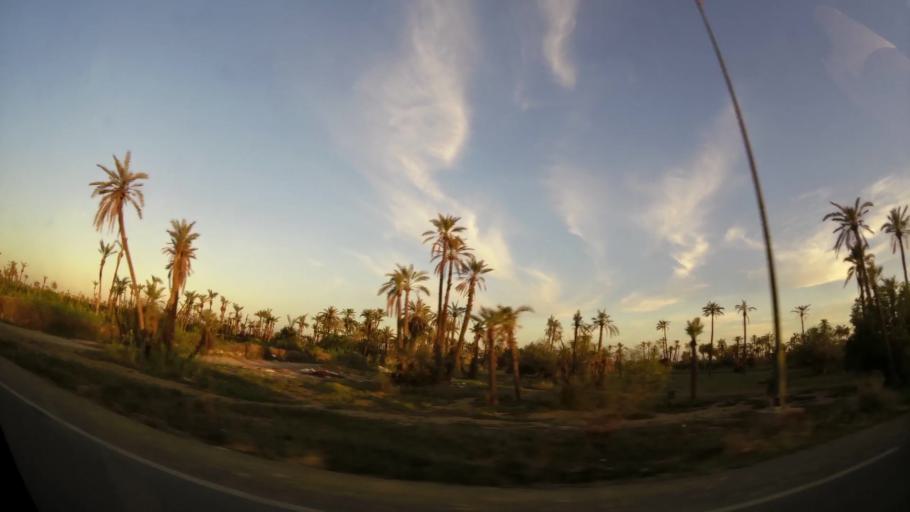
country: MA
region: Marrakech-Tensift-Al Haouz
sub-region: Marrakech
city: Marrakesh
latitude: 31.6884
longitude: -8.0210
